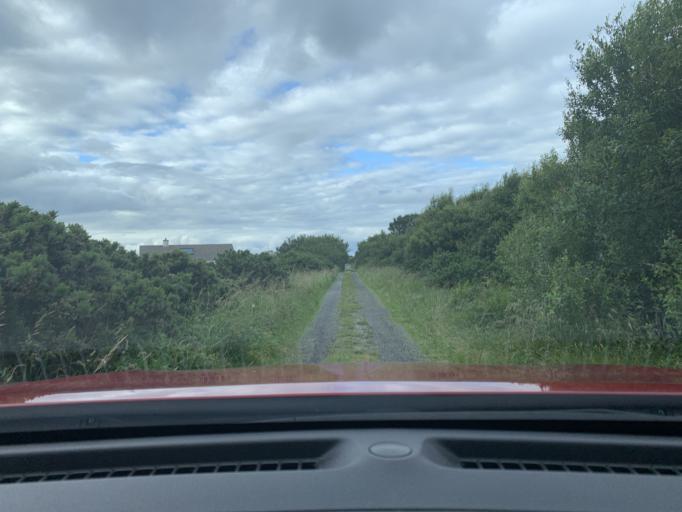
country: IE
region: Connaught
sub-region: County Leitrim
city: Kinlough
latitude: 54.4586
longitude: -8.3564
